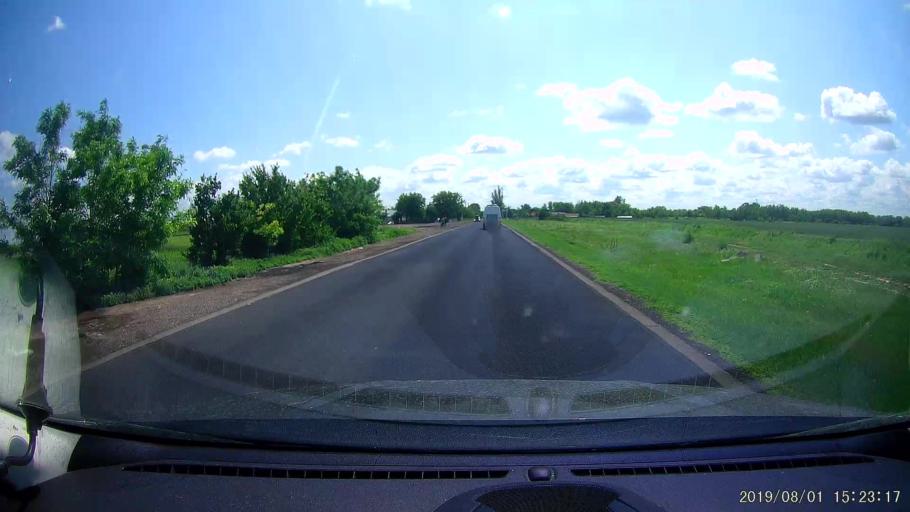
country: RO
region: Braila
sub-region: Comuna Viziru
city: Lanurile
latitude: 45.0426
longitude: 27.7620
